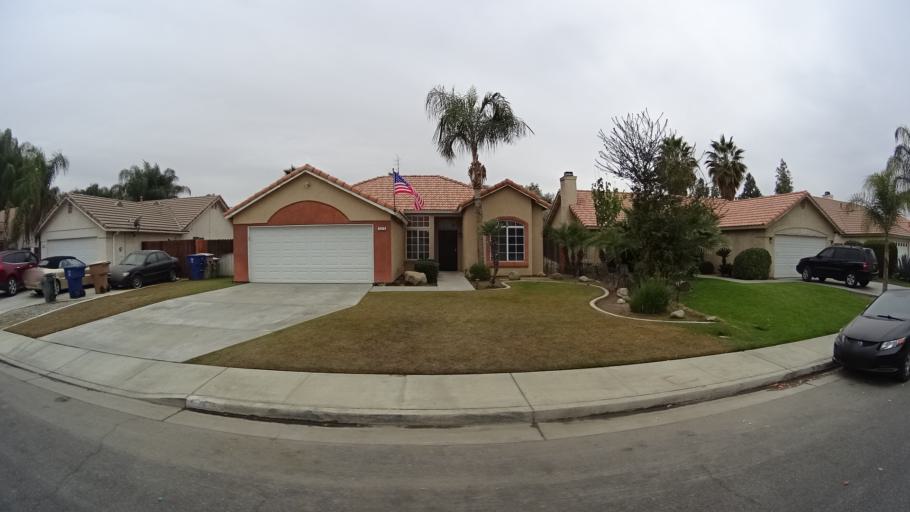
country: US
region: California
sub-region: Kern County
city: Greenfield
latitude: 35.2880
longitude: -119.0463
